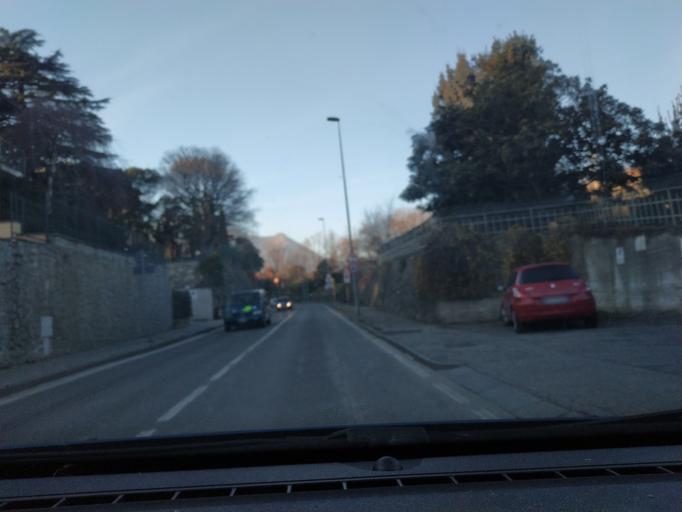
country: IT
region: Piedmont
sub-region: Provincia di Torino
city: Ivrea
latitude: 45.4698
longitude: 7.8698
